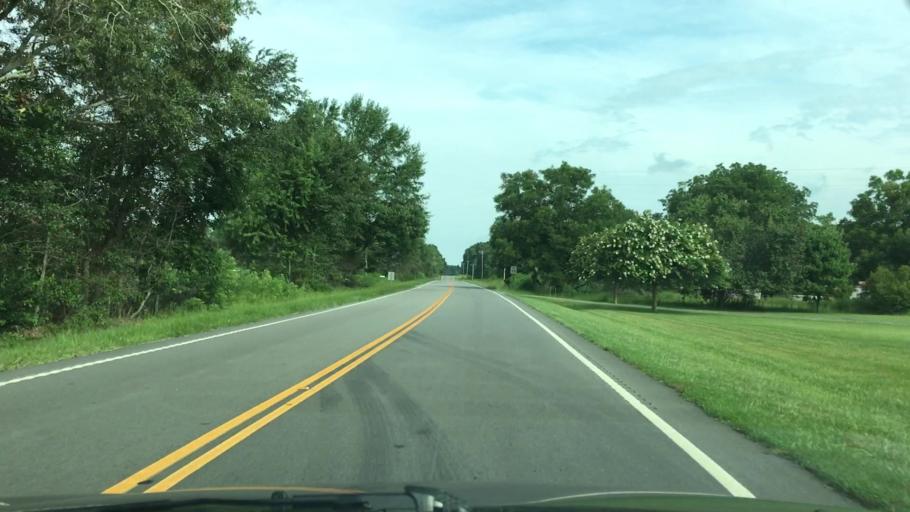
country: US
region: South Carolina
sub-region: Lexington County
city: Batesburg-Leesville
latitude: 33.7042
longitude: -81.4841
